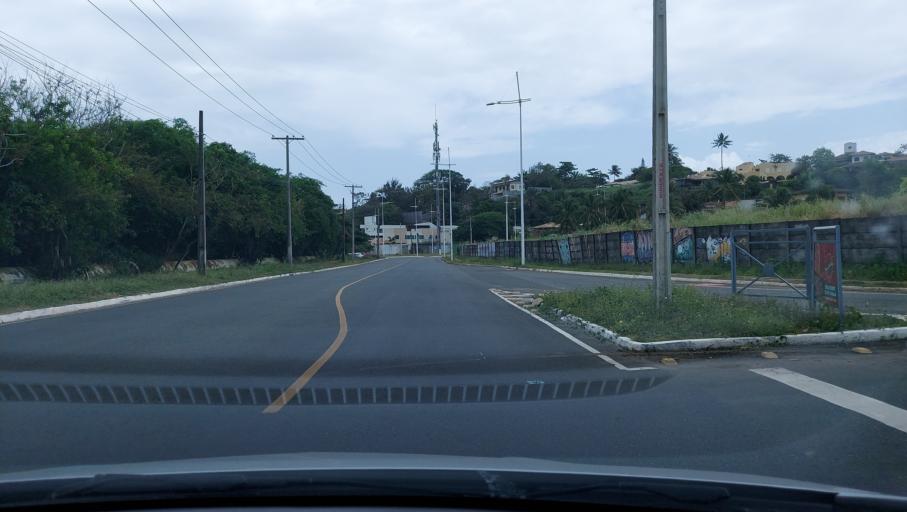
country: BR
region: Bahia
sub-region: Lauro De Freitas
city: Lauro de Freitas
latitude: -12.9519
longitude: -38.3936
